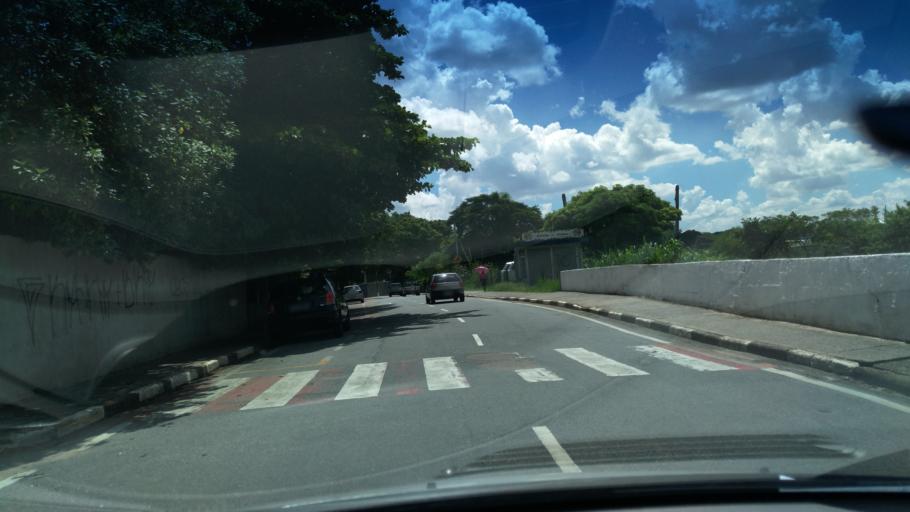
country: BR
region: Sao Paulo
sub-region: Vinhedo
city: Vinhedo
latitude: -23.0255
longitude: -46.9794
